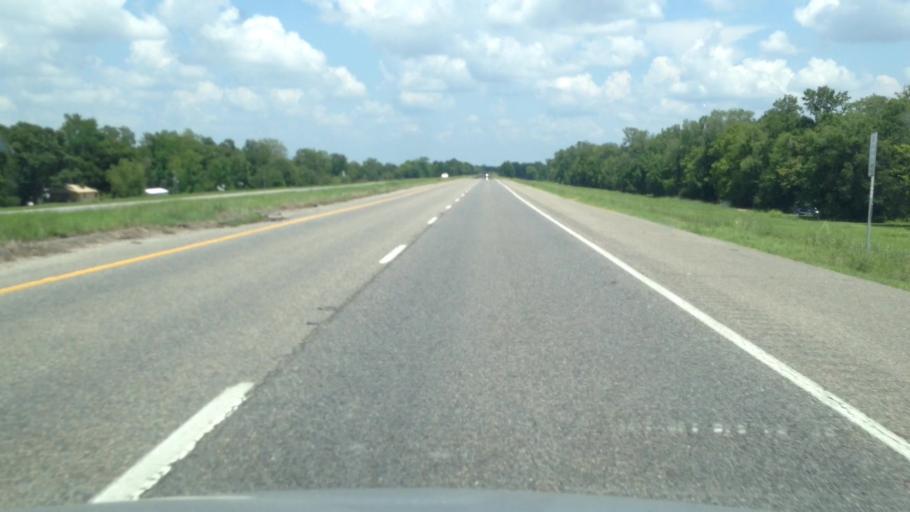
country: US
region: Louisiana
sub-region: Saint Landry Parish
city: Krotz Springs
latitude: 30.5487
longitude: -91.8467
